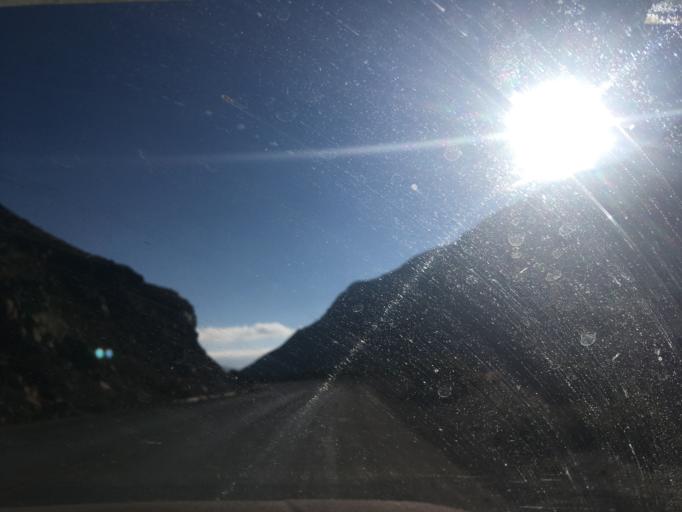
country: BO
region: La Paz
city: Quime
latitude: -17.0201
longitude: -67.2805
